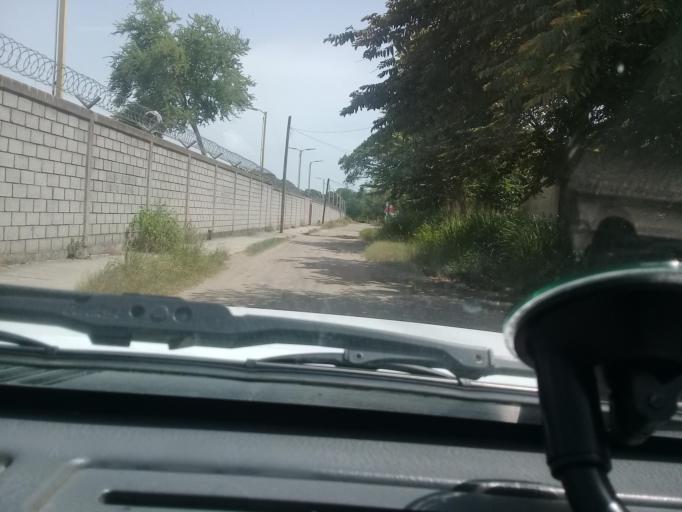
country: MX
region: Veracruz
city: Anahuac
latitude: 22.2291
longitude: -97.8325
